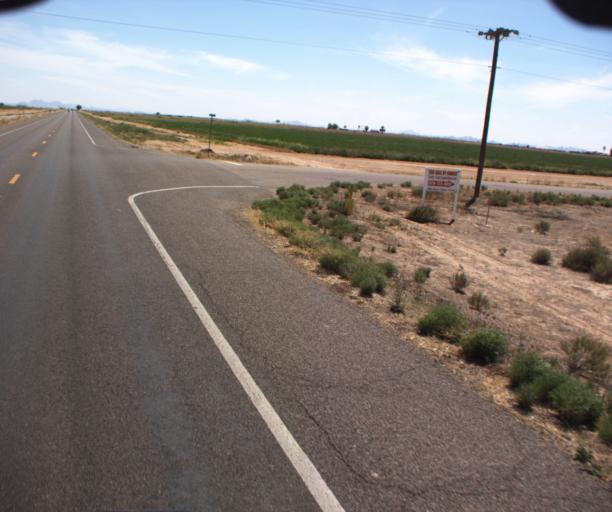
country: US
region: Arizona
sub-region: Pinal County
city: Coolidge
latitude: 32.8654
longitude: -111.5152
